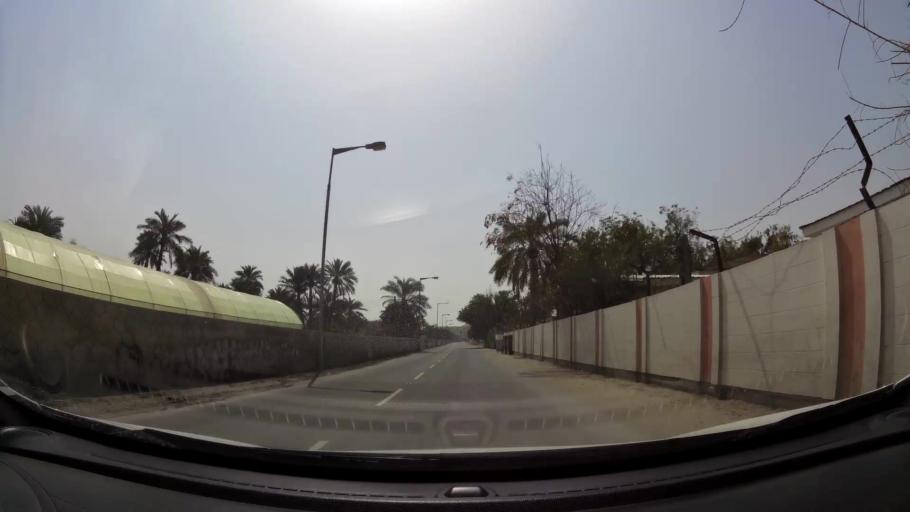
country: BH
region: Manama
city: Jidd Hafs
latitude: 26.2249
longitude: 50.5040
